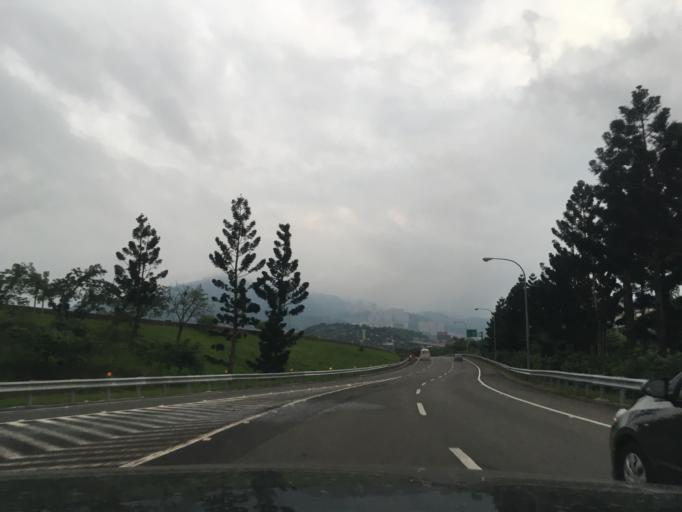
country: TW
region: Taipei
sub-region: Taipei
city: Banqiao
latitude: 24.9686
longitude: 121.5221
